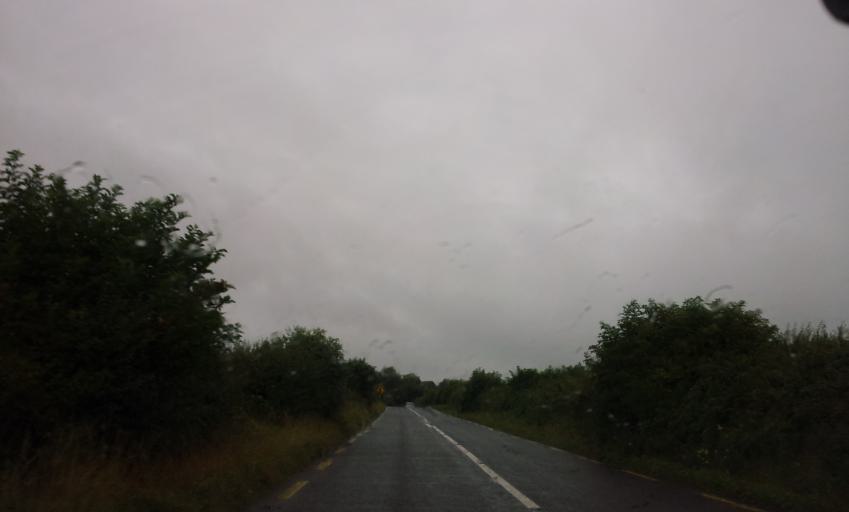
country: IE
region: Munster
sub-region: County Cork
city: Mallow
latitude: 52.1615
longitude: -8.5897
